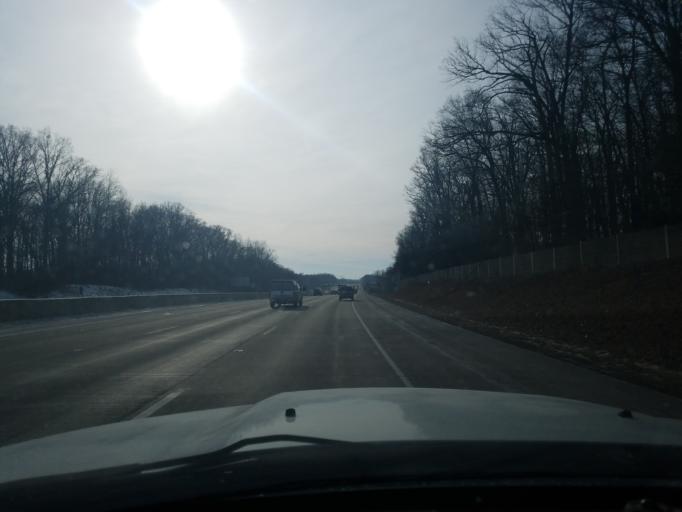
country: US
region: Indiana
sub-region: Allen County
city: Fort Wayne
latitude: 41.0660
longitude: -85.2324
